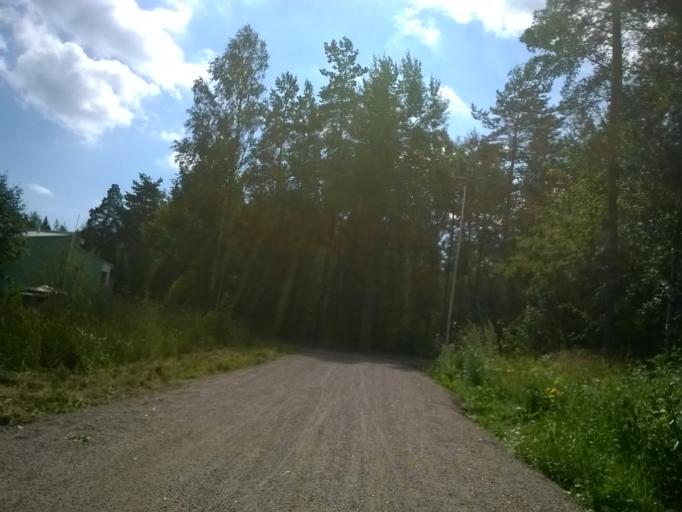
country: FI
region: Uusimaa
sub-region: Helsinki
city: Teekkarikylae
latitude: 60.2569
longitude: 24.8949
